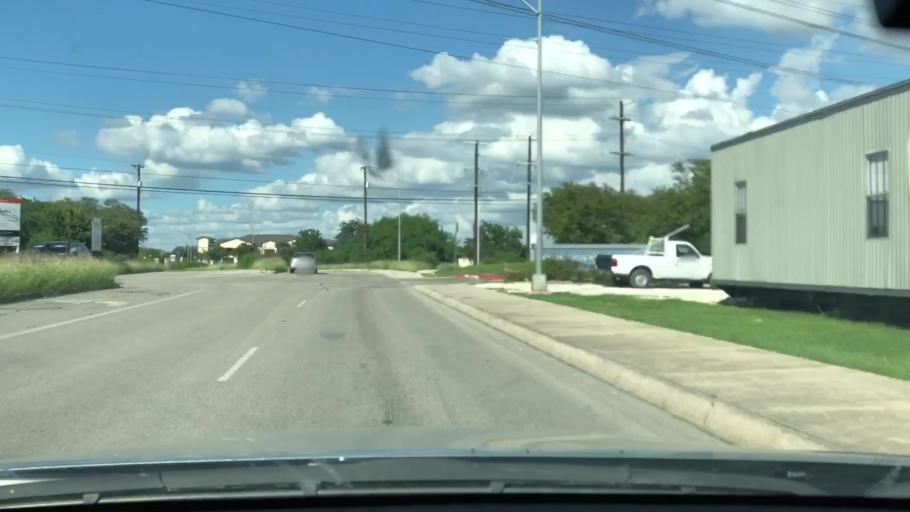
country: US
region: Texas
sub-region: Bexar County
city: Hollywood Park
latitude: 29.6166
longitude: -98.4768
